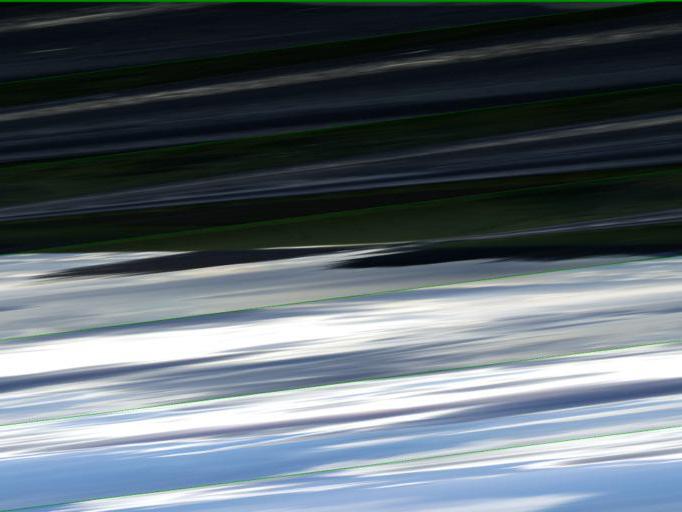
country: FR
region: Ile-de-France
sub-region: Departement du Val-d'Oise
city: Magny-en-Vexin
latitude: 49.1854
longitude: 1.8467
